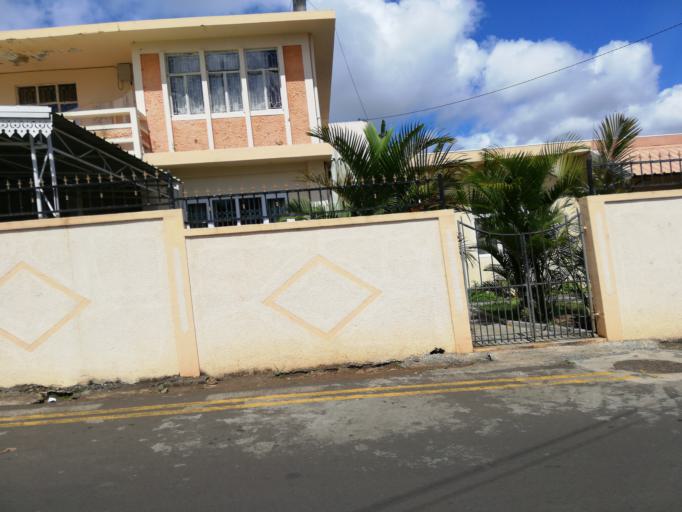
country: MU
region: Moka
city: Moka
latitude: -20.2132
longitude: 57.4706
